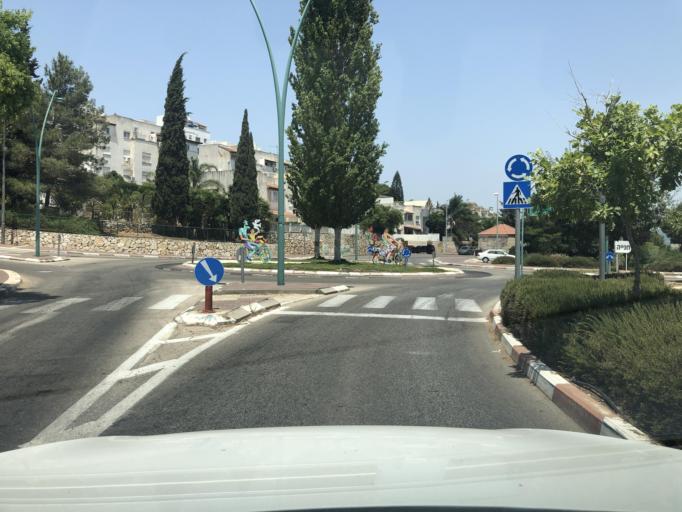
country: IL
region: Haifa
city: Daliyat el Karmil
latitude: 32.6464
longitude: 35.0919
